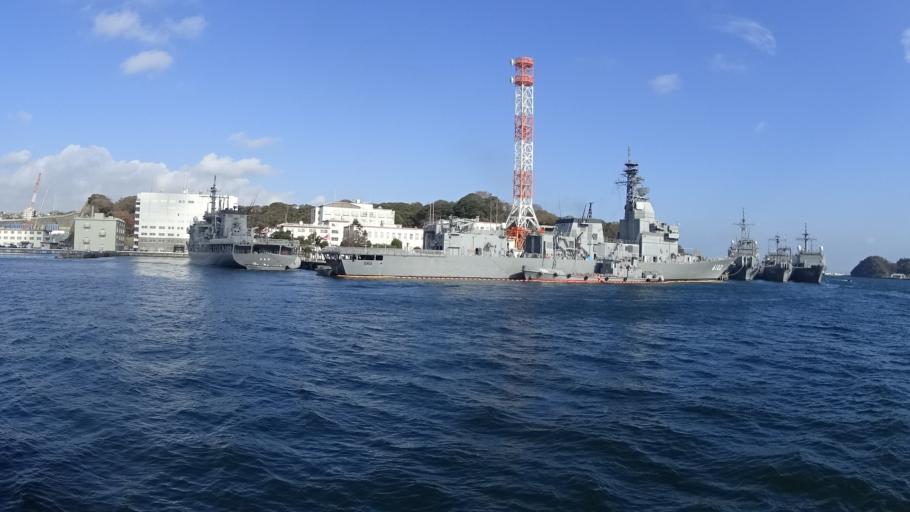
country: JP
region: Kanagawa
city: Yokosuka
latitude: 35.2993
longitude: 139.6371
